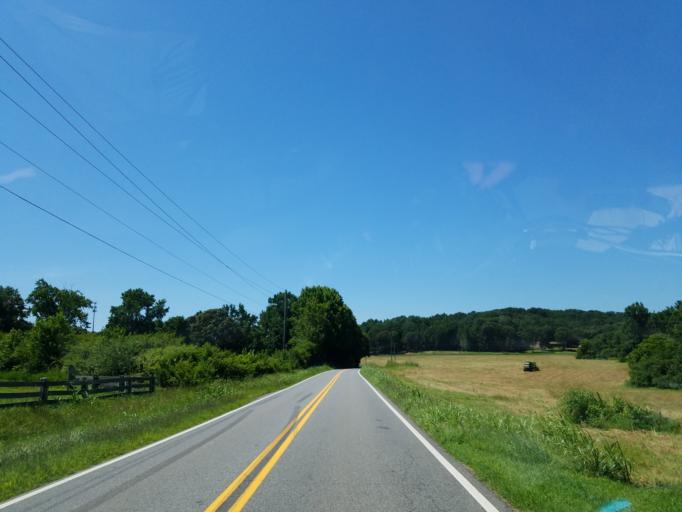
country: US
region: Georgia
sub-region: Forsyth County
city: Cumming
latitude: 34.2645
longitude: -84.0729
